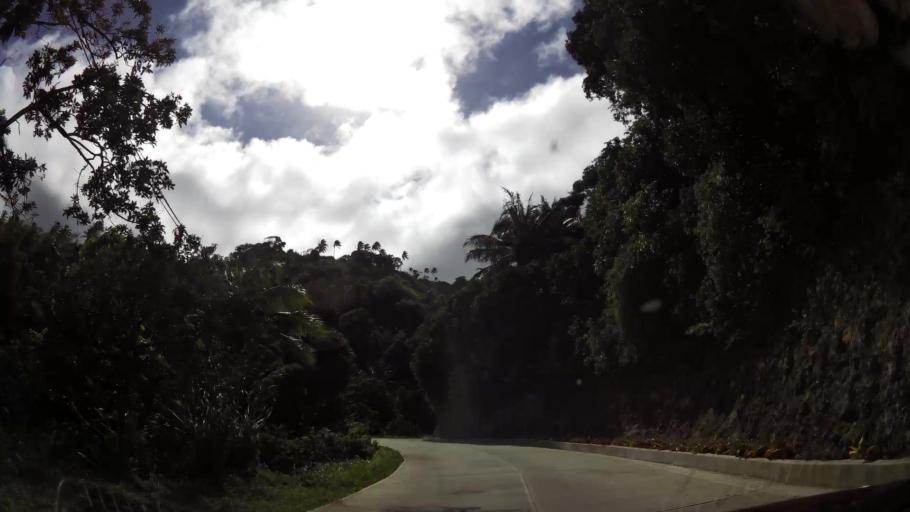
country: DM
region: Saint John
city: Portsmouth
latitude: 15.6269
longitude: -61.4225
